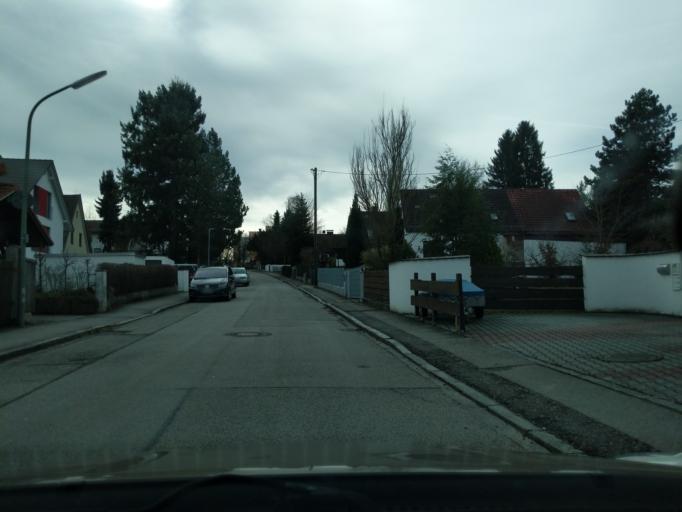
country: DE
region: Bavaria
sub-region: Upper Bavaria
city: Zorneding
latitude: 48.0887
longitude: 11.8324
